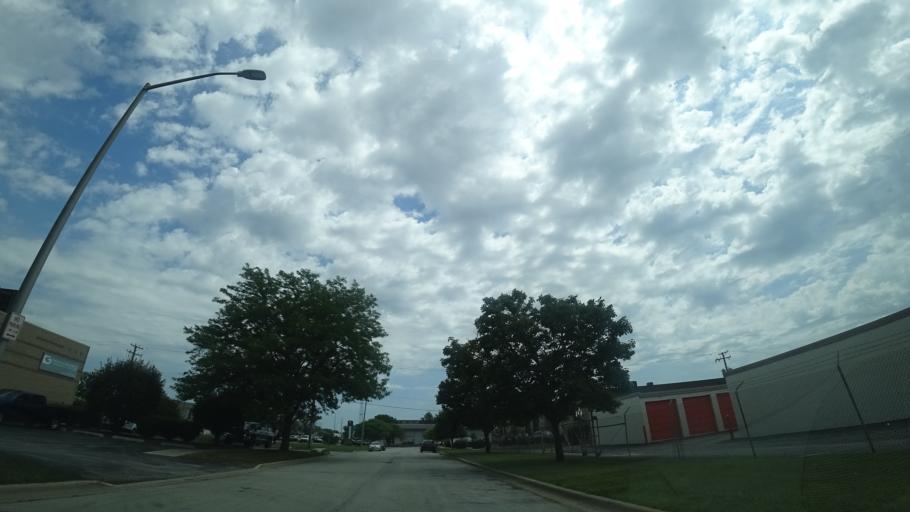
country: US
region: Illinois
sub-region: Cook County
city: Crestwood
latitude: 41.6640
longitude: -87.7475
